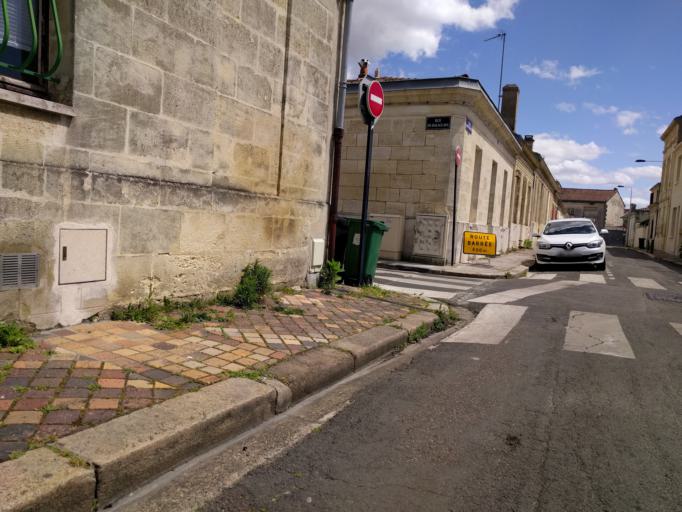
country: FR
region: Aquitaine
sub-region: Departement de la Gironde
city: Bordeaux
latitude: 44.8223
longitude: -0.5778
